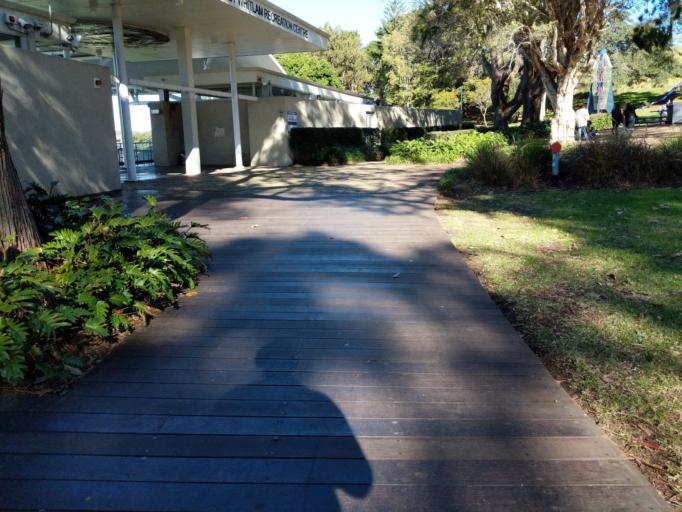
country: AU
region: New South Wales
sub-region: Waverley
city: Bondi
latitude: -33.8939
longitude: 151.2577
